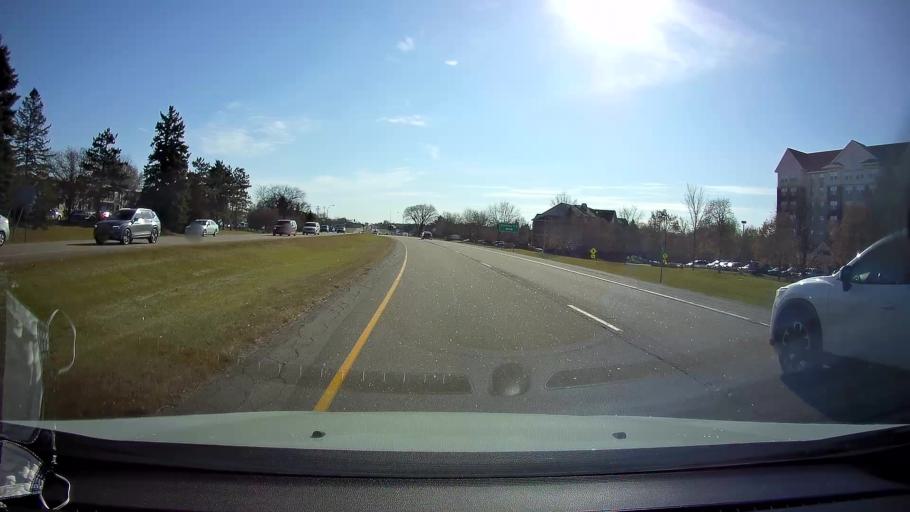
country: US
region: Minnesota
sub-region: Ramsey County
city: Arden Hills
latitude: 45.0302
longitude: -93.1670
